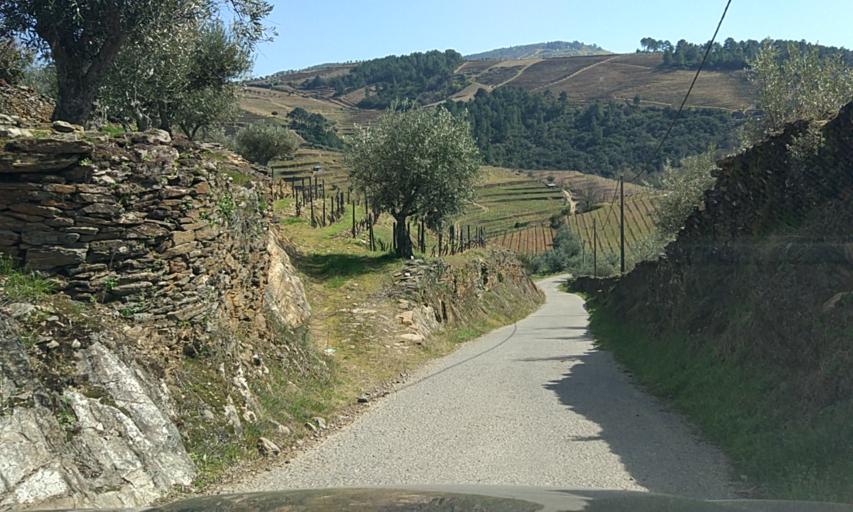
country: PT
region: Vila Real
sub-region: Sabrosa
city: Sabrosa
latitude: 41.3087
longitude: -7.5506
